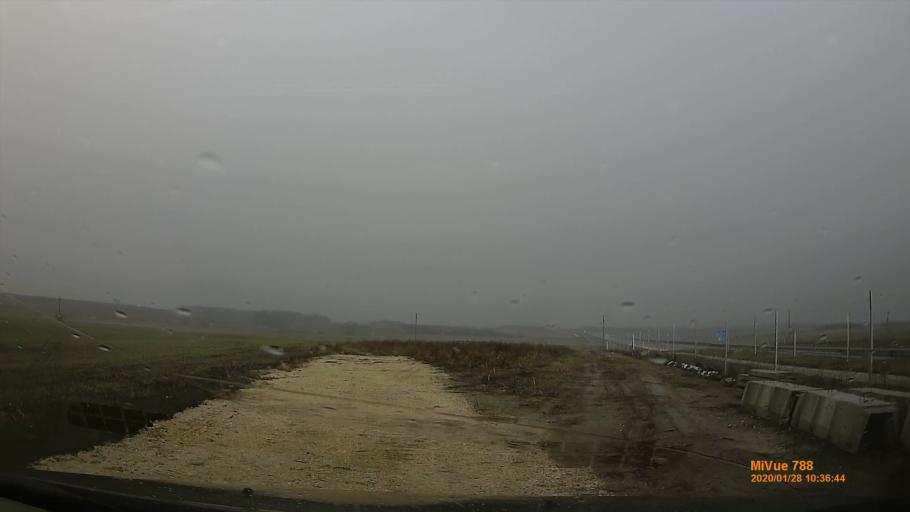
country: HU
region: Pest
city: Monor
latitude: 47.3545
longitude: 19.4893
